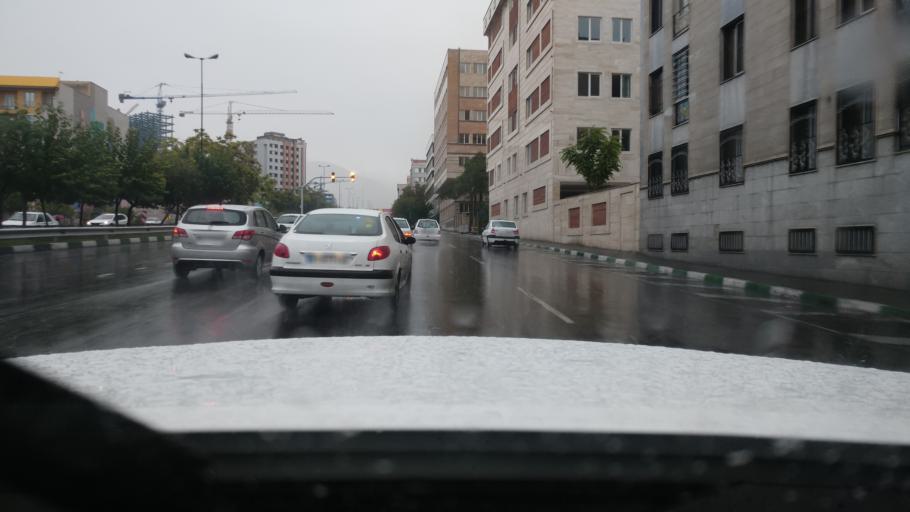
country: IR
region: Tehran
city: Tehran
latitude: 35.7219
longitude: 51.3086
